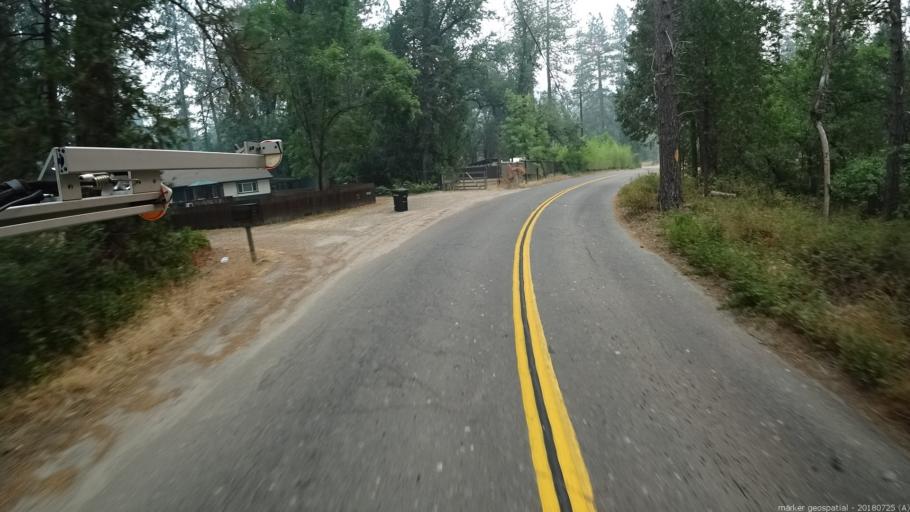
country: US
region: California
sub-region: Madera County
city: Oakhurst
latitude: 37.3664
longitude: -119.6106
